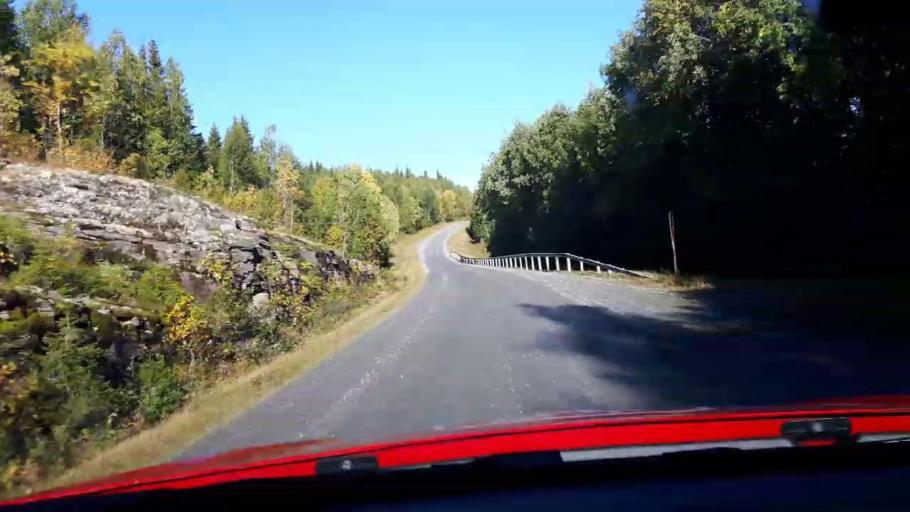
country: NO
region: Nord-Trondelag
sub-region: Lierne
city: Sandvika
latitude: 64.5783
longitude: 13.8945
